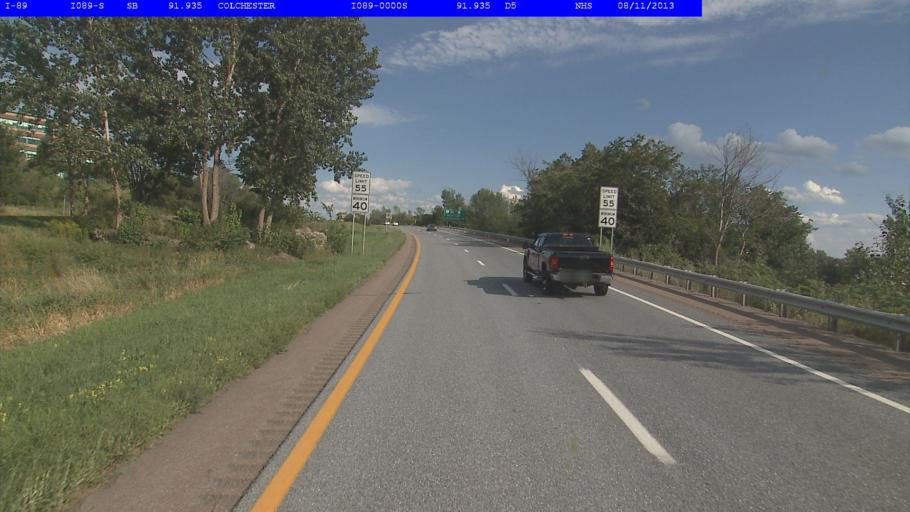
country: US
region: Vermont
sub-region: Chittenden County
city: Winooski
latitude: 44.5090
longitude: -73.1891
